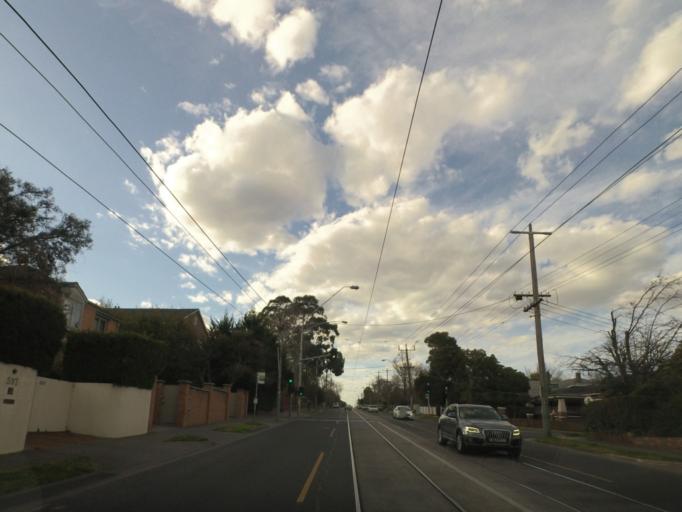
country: AU
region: Victoria
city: Glenferrie
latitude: -37.8406
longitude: 145.0549
